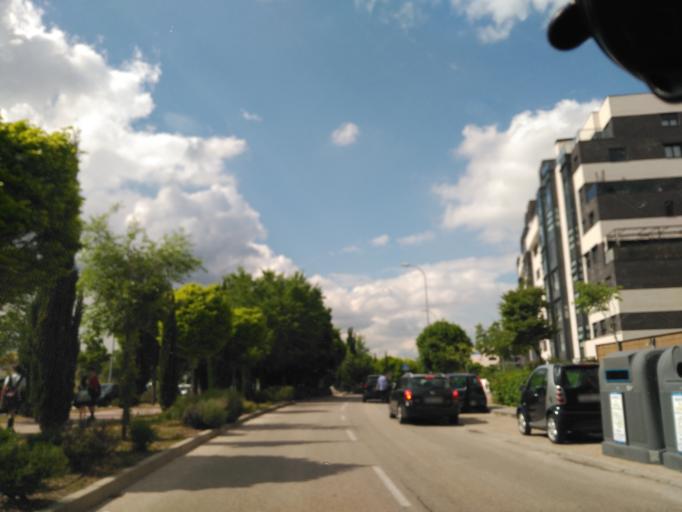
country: ES
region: Madrid
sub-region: Provincia de Madrid
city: Pinar de Chamartin
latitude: 40.4922
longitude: -3.6658
